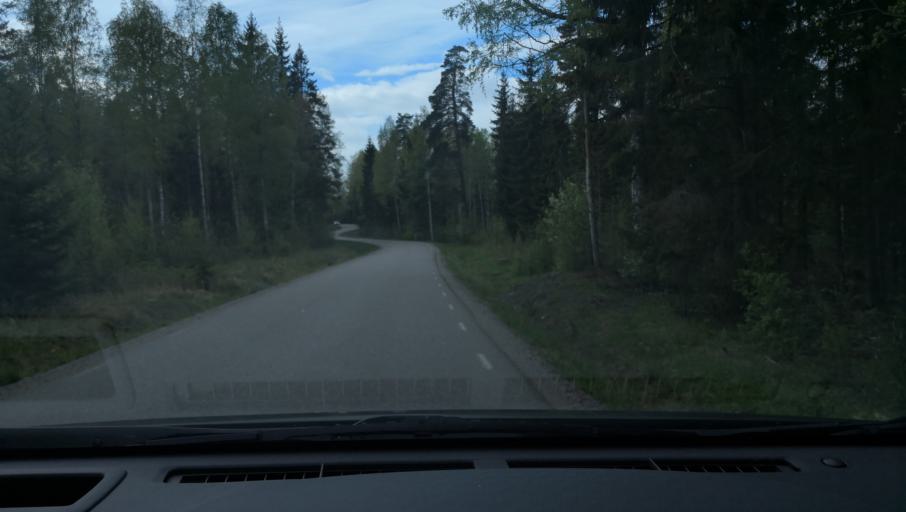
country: SE
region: OErebro
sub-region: Kumla Kommun
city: Hallabrottet
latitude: 59.1564
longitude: 15.1942
